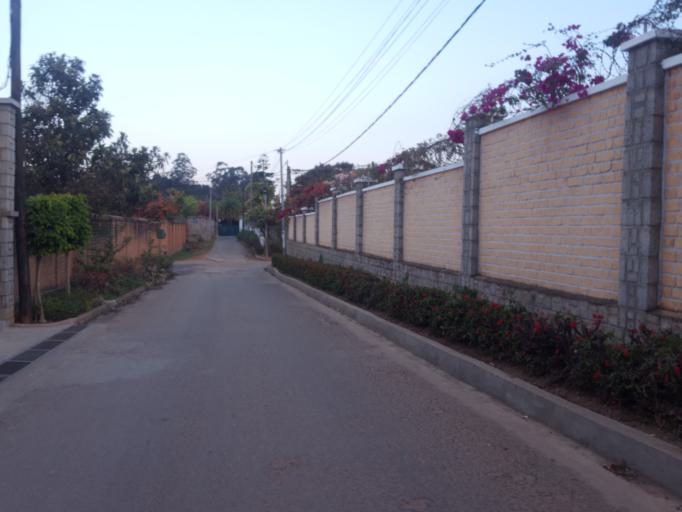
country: MG
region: Analamanga
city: Antananarivo
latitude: -18.8683
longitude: 47.5335
